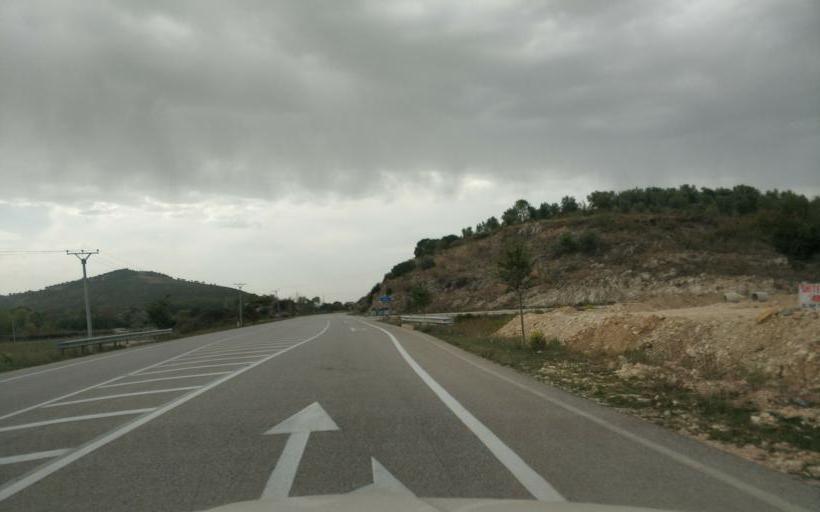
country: AL
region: Fier
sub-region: Rrethi i Mallakastres
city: Kute
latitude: 40.5140
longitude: 19.7466
